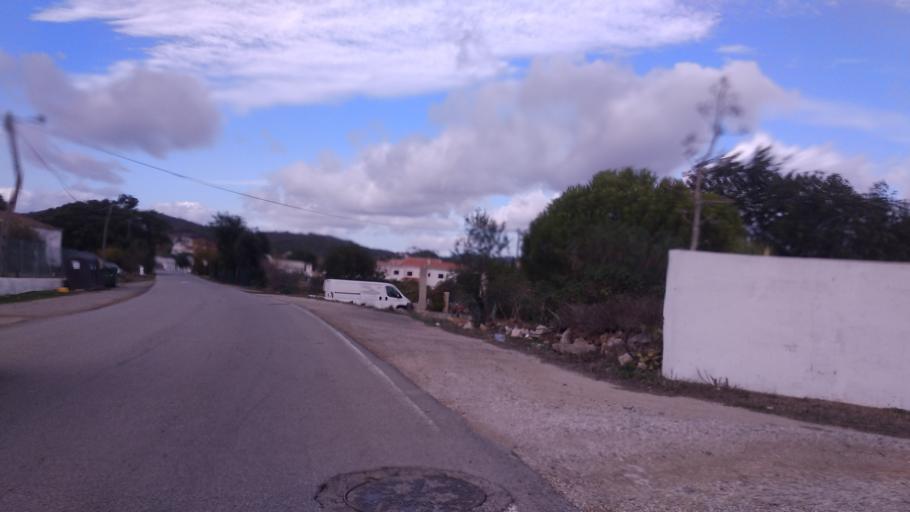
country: PT
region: Faro
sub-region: Sao Bras de Alportel
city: Sao Bras de Alportel
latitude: 37.1665
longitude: -7.9049
